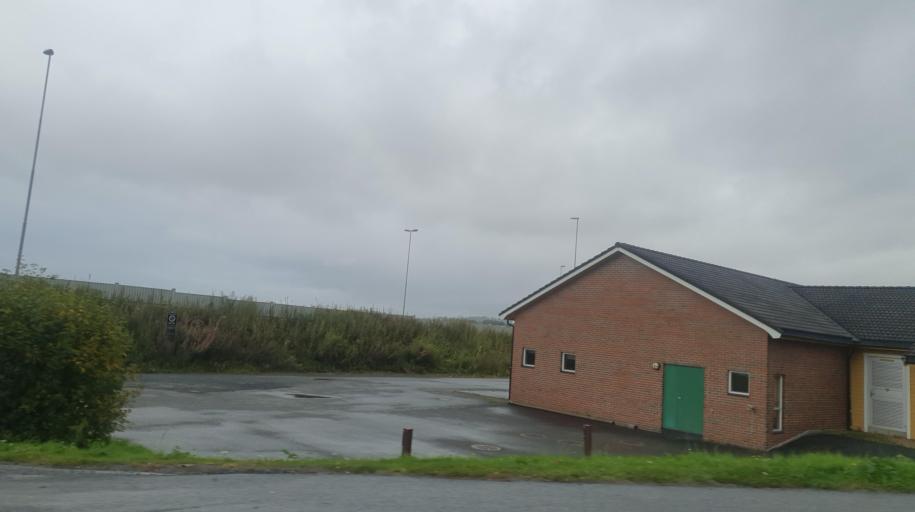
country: NO
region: Nord-Trondelag
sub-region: Levanger
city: Skogn
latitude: 63.7103
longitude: 11.1871
